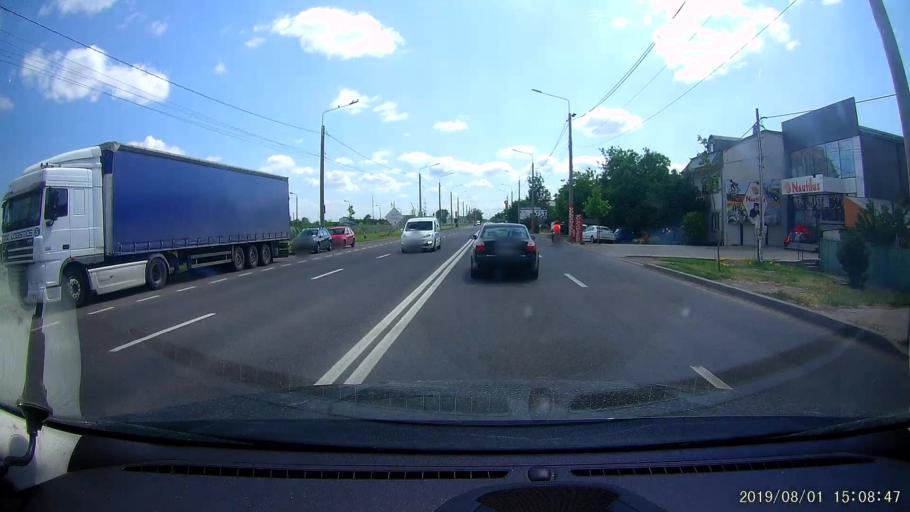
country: RO
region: Braila
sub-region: Municipiul Braila
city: Braila
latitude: 45.2388
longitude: 27.9430
